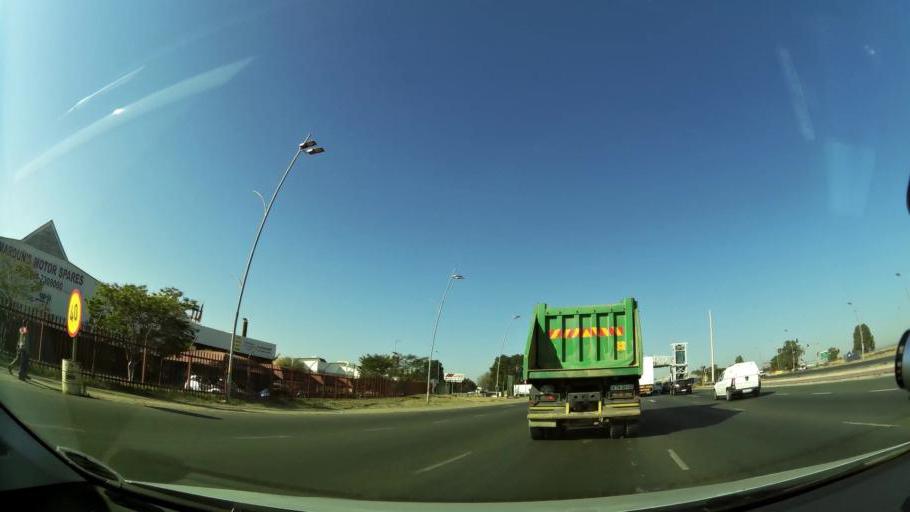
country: ZA
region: Gauteng
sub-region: City of Johannesburg Metropolitan Municipality
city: Modderfontein
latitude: -26.0683
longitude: 28.1860
